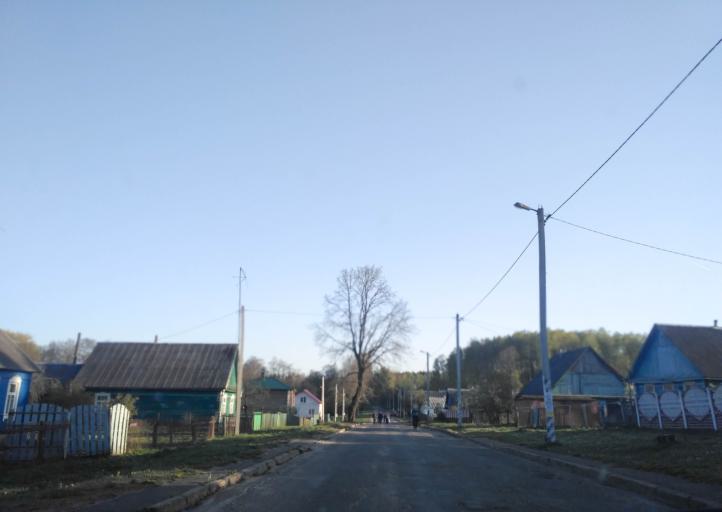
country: BY
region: Minsk
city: Pyatryshki
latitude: 54.0961
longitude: 27.1951
